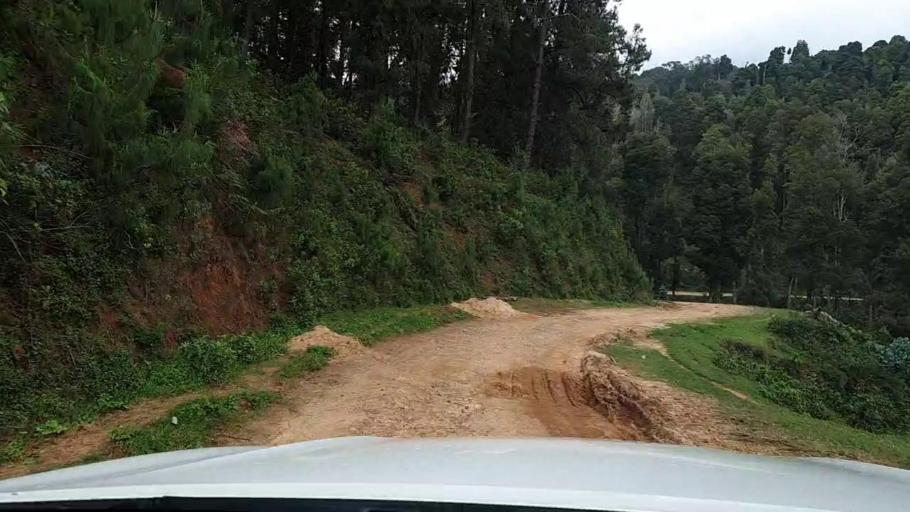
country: RW
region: Western Province
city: Kibuye
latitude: -2.2906
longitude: 29.3698
